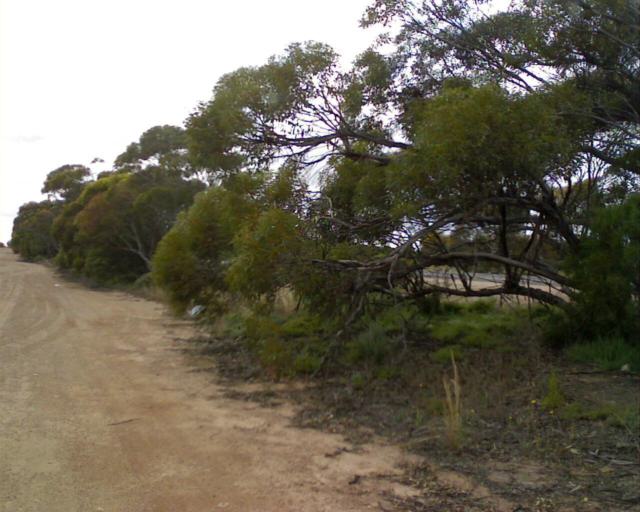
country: AU
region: South Australia
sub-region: Ceduna
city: Ceduna
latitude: -32.1433
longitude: 133.8747
